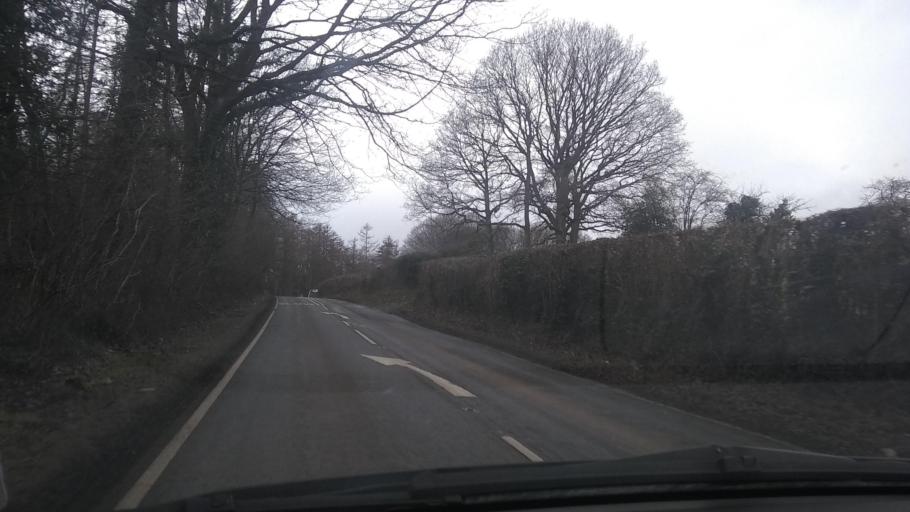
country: GB
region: England
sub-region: Shropshire
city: Cleobury Mortimer
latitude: 52.3764
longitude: -2.4319
